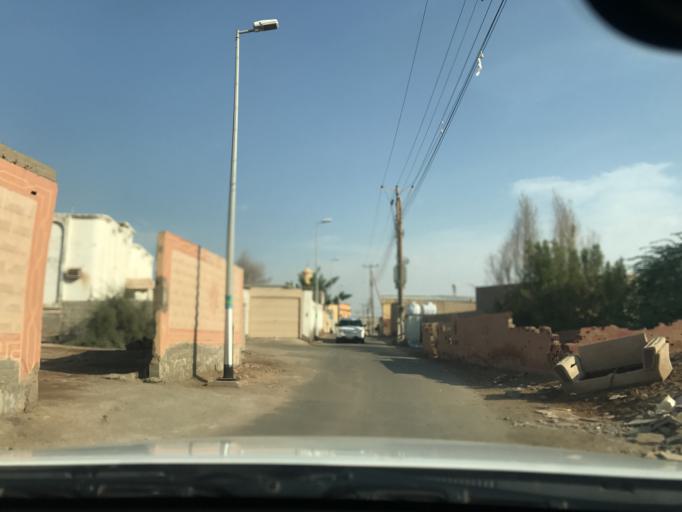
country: SA
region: Makkah
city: Al Jumum
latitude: 21.4459
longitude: 39.5337
